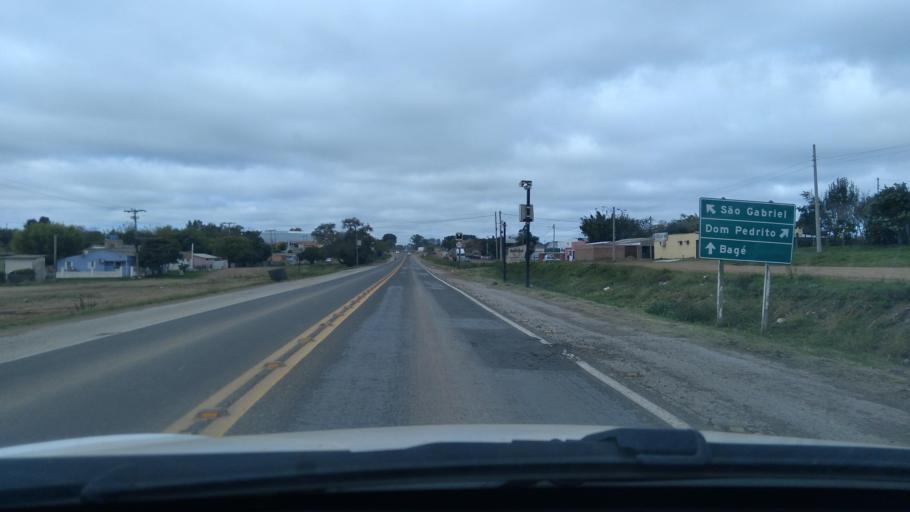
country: BR
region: Rio Grande do Sul
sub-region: Dom Pedrito
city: Dom Pedrito
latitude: -30.9655
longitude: -54.6675
